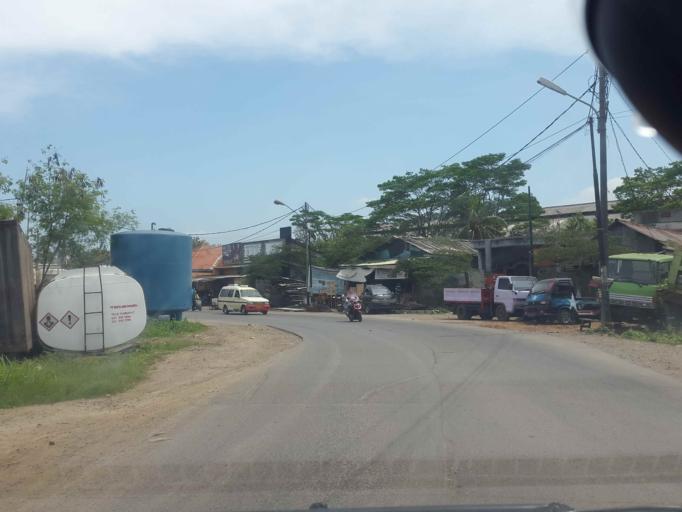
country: ID
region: Banten
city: Tangerang
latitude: -6.1544
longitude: 106.6600
